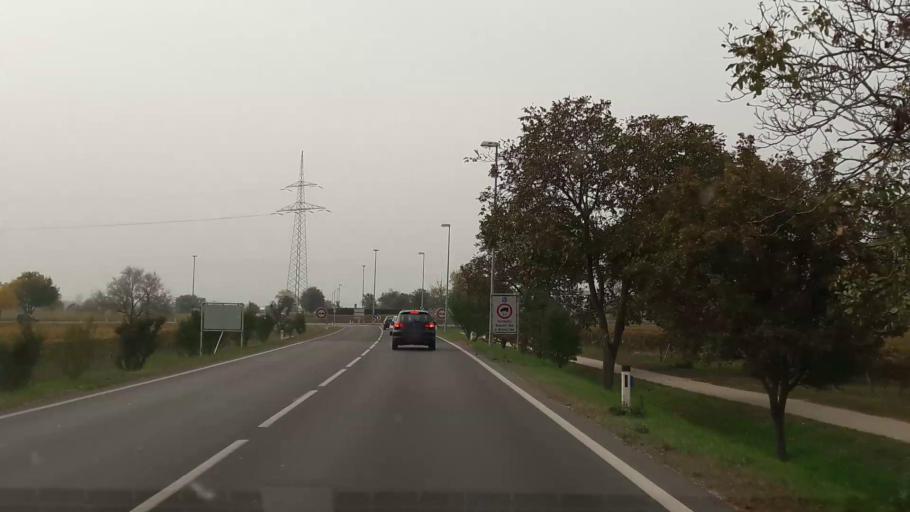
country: AT
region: Burgenland
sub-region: Politischer Bezirk Neusiedl am See
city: Gols
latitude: 47.9108
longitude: 16.8906
